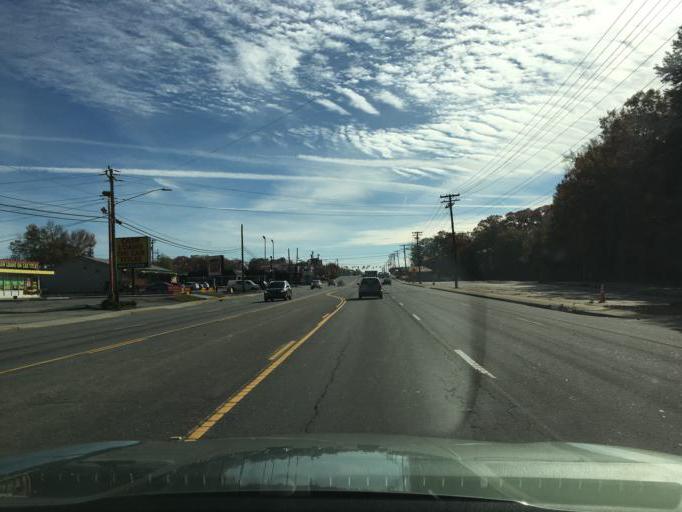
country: US
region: South Carolina
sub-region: Greenville County
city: Greenville
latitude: 34.8724
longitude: -82.3591
